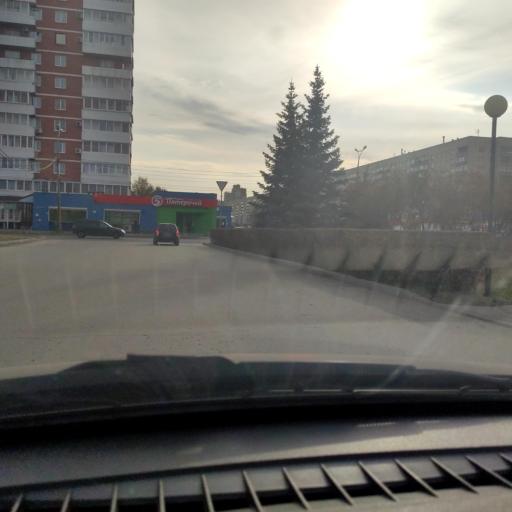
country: RU
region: Samara
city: Tol'yatti
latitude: 53.5068
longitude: 49.4204
